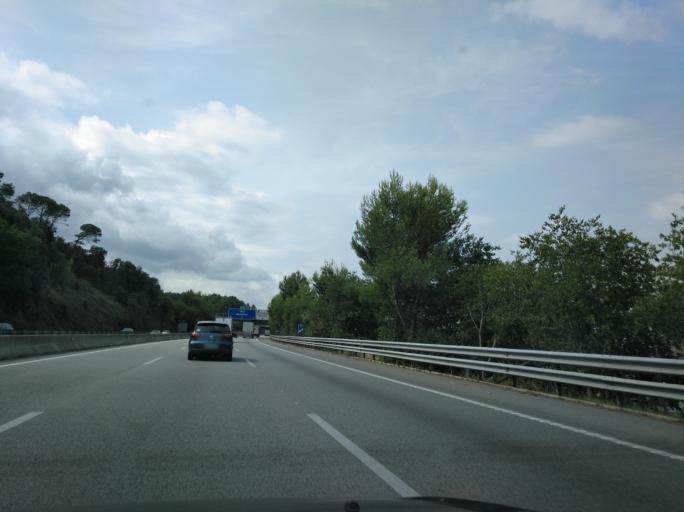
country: ES
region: Catalonia
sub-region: Provincia de Barcelona
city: Sant Celoni
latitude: 41.6772
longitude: 2.4874
